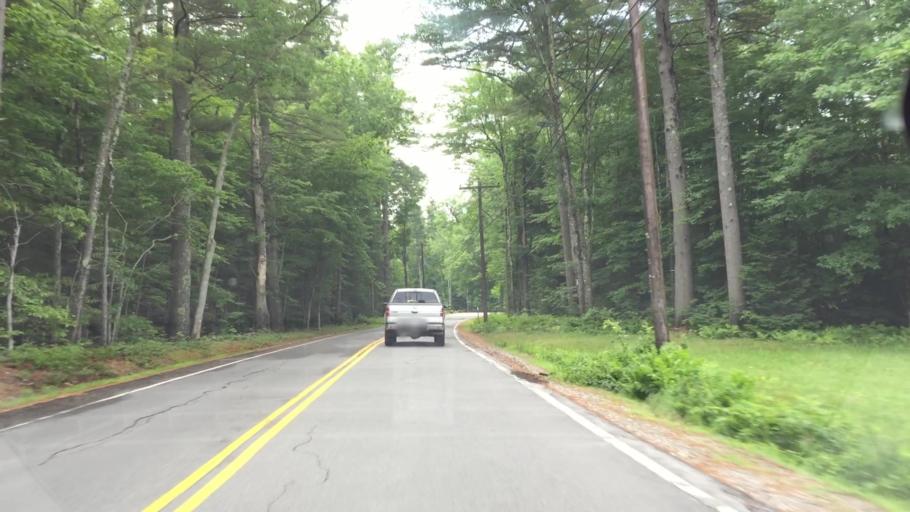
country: US
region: New Hampshire
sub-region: Grafton County
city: Holderness
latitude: 43.7538
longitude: -71.5549
